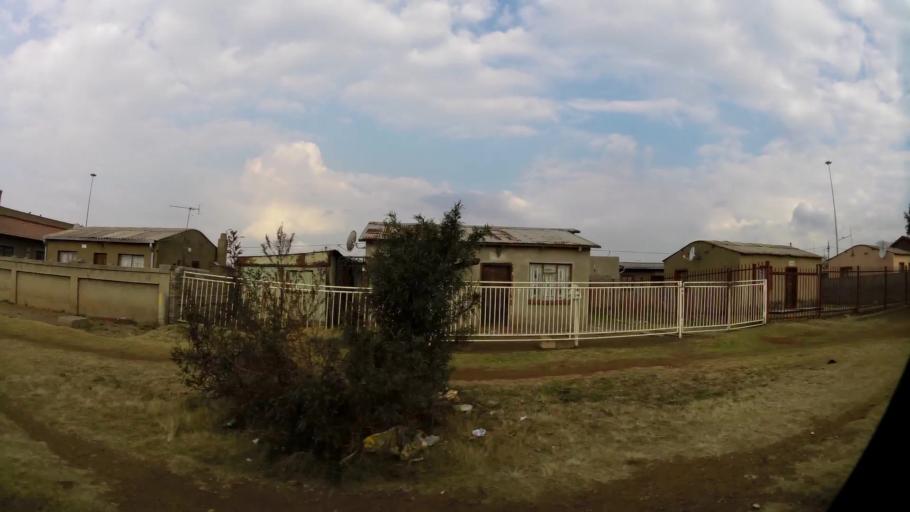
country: ZA
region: Gauteng
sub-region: Sedibeng District Municipality
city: Vereeniging
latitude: -26.6767
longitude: 27.8756
